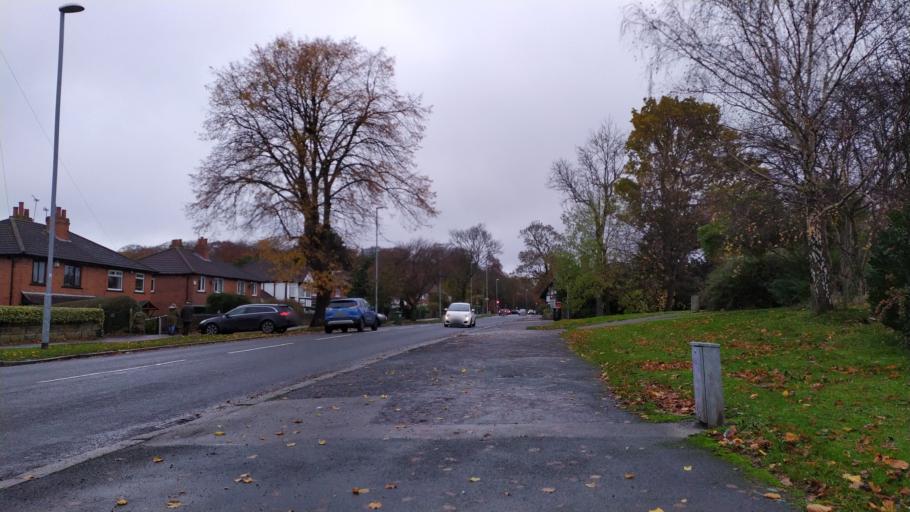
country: GB
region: England
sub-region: City and Borough of Leeds
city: Chapel Allerton
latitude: 53.8315
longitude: -1.5622
